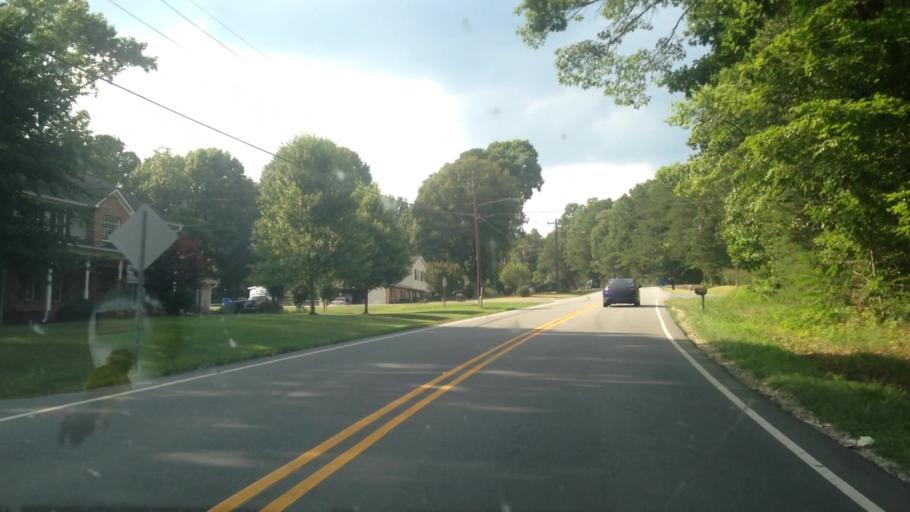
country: US
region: North Carolina
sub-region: Forsyth County
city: Kernersville
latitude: 36.1299
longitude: -80.1162
